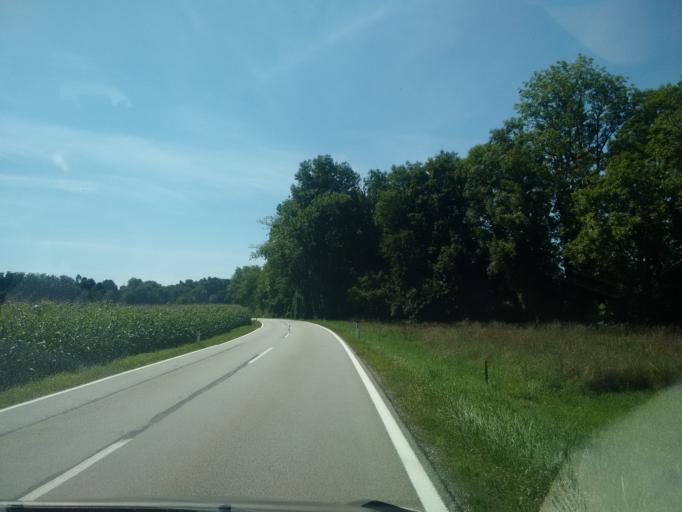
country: DE
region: Bavaria
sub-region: Lower Bavaria
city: Kirchdorf am Inn
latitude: 48.2130
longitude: 12.9742
